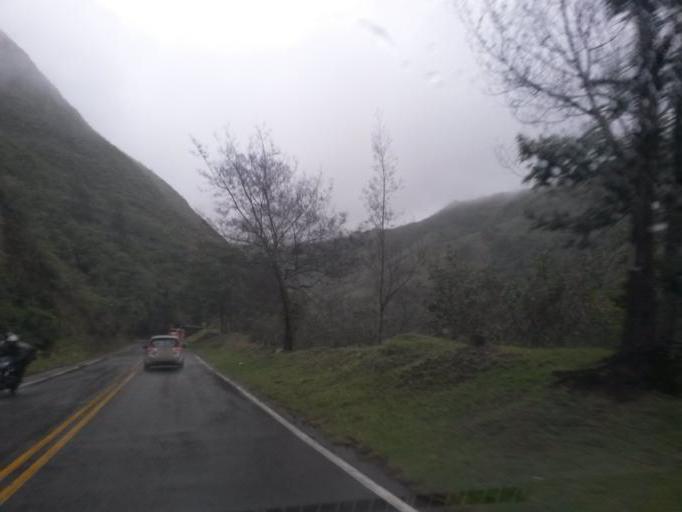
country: CO
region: Cauca
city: Popayan
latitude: 2.3830
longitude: -76.4959
